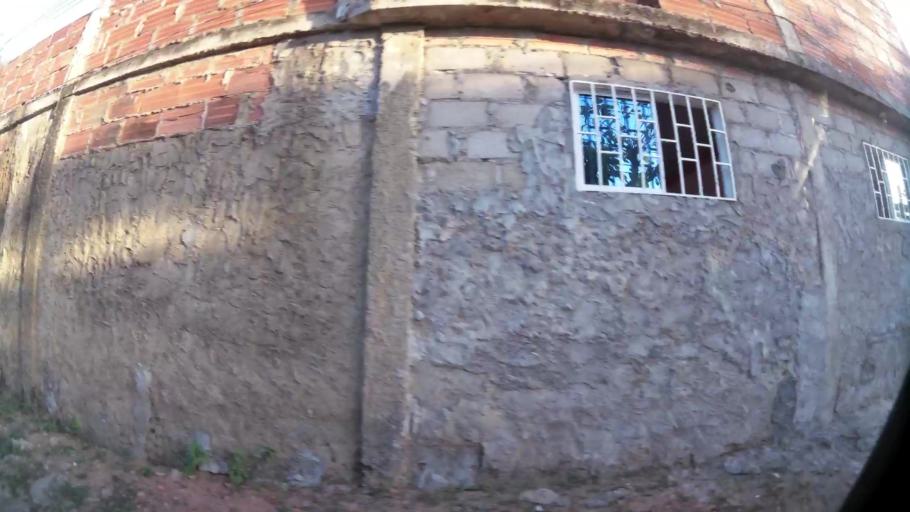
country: CO
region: Bolivar
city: Cartagena
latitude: 10.4104
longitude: -75.4553
